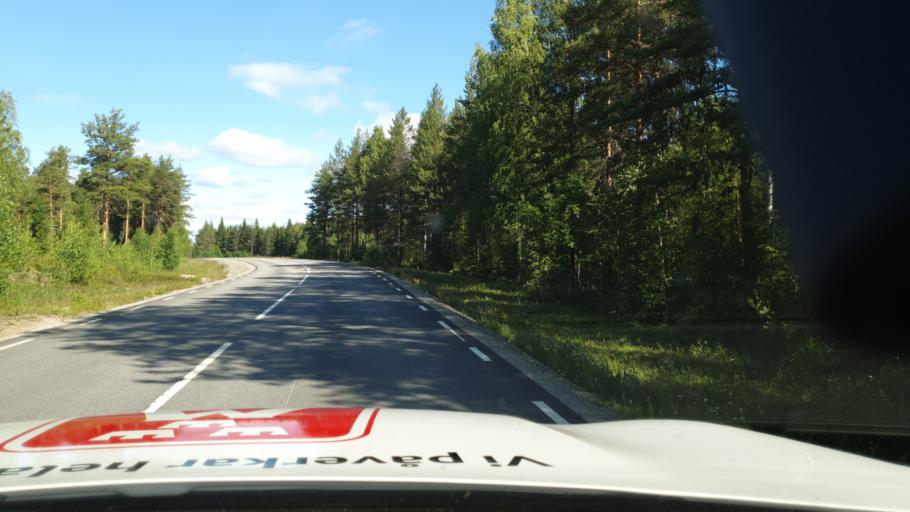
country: SE
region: Vaesterbotten
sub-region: Norsjo Kommun
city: Norsjoe
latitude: 64.6437
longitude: 19.2861
